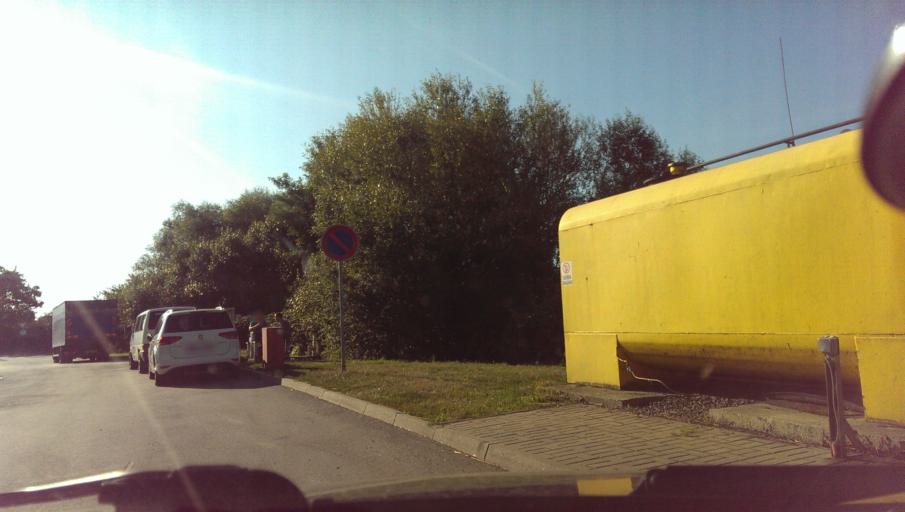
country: CZ
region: Olomoucky
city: Hustopece Nad Becvou
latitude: 49.5310
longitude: 17.8629
